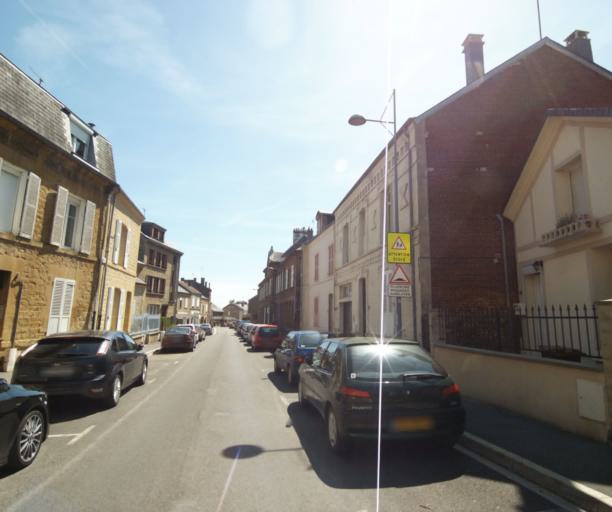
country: FR
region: Champagne-Ardenne
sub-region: Departement des Ardennes
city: Charleville-Mezieres
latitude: 49.7538
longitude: 4.7274
